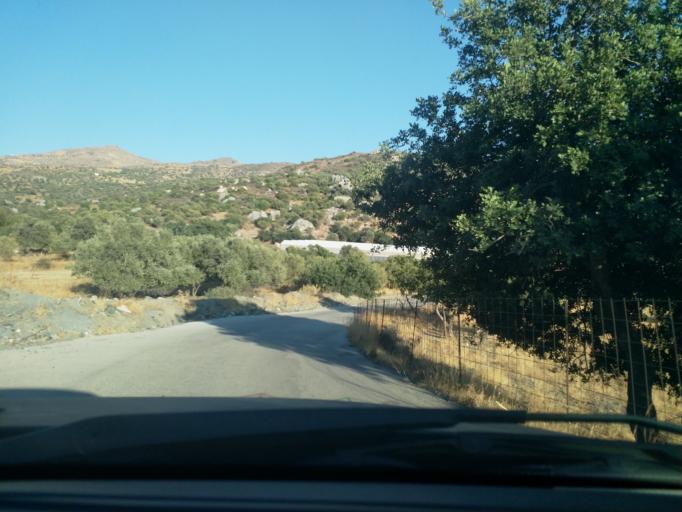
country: GR
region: Crete
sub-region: Nomos Rethymnis
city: Agia Galini
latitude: 35.1160
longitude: 24.5651
